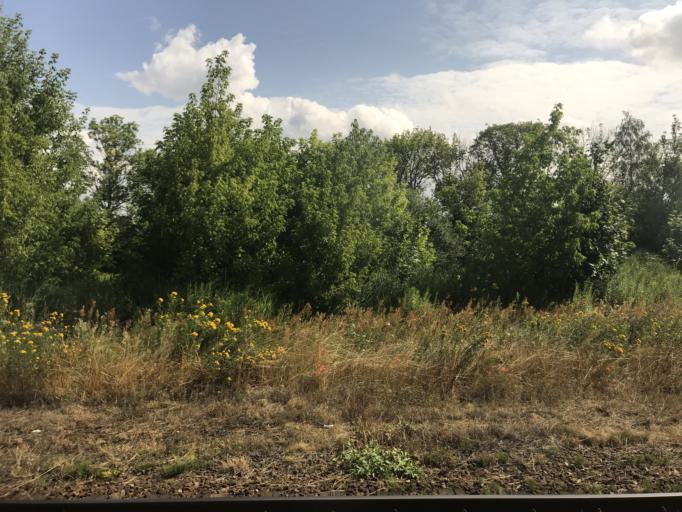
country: PL
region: Kujawsko-Pomorskie
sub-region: Powiat inowroclawski
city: Zlotniki Kujawskie
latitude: 52.9036
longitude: 18.1475
